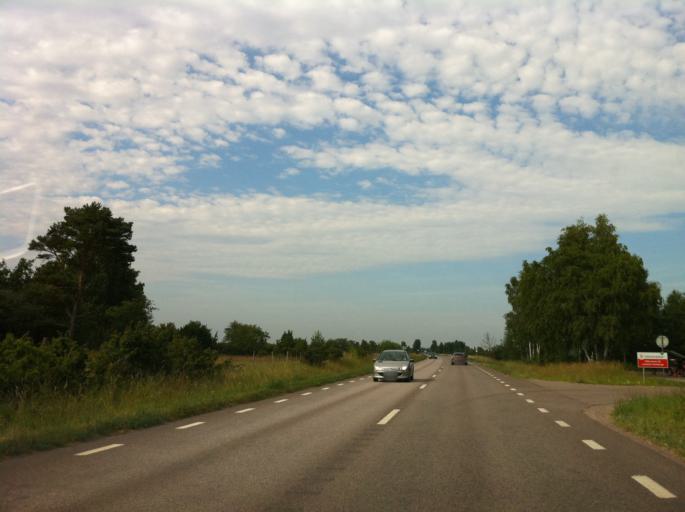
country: SE
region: Kalmar
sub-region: Borgholms Kommun
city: Borgholm
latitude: 56.9257
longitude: 16.7628
